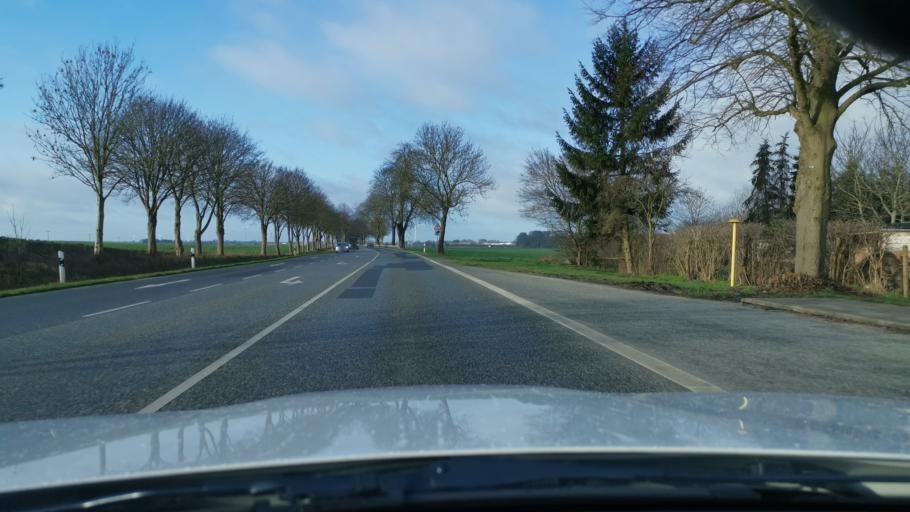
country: DE
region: Mecklenburg-Vorpommern
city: Laage
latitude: 53.8970
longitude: 12.2784
